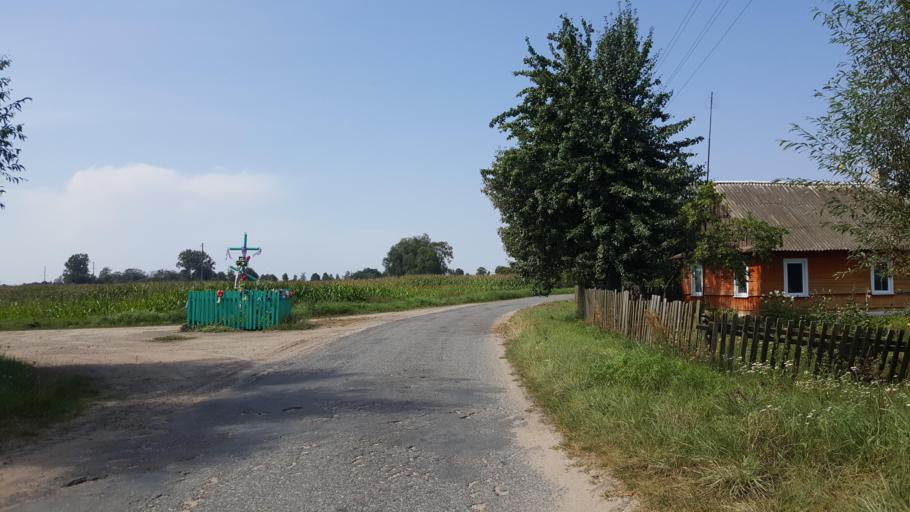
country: PL
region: Podlasie
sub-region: Powiat hajnowski
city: Czeremcha
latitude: 52.4938
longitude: 23.5724
